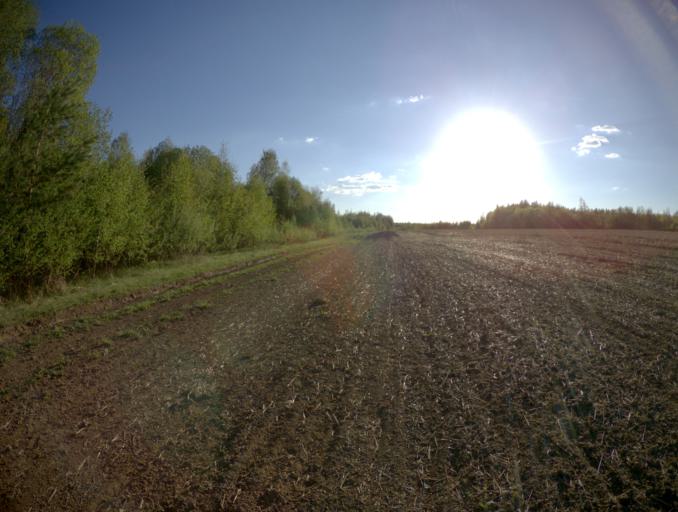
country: RU
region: Ivanovo
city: Gavrilov Posad
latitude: 56.3912
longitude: 40.1118
